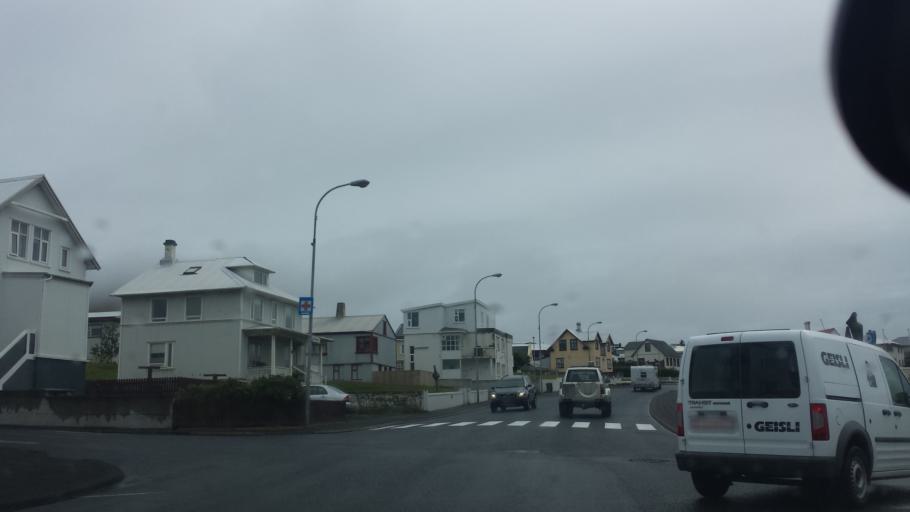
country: IS
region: South
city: Vestmannaeyjar
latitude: 63.4400
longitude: -20.2666
